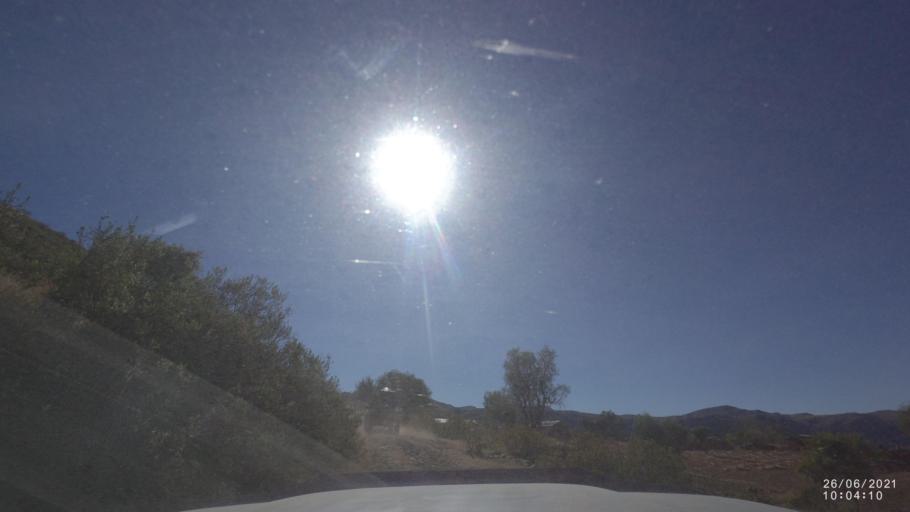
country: BO
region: Cochabamba
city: Mizque
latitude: -17.9237
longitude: -65.6272
